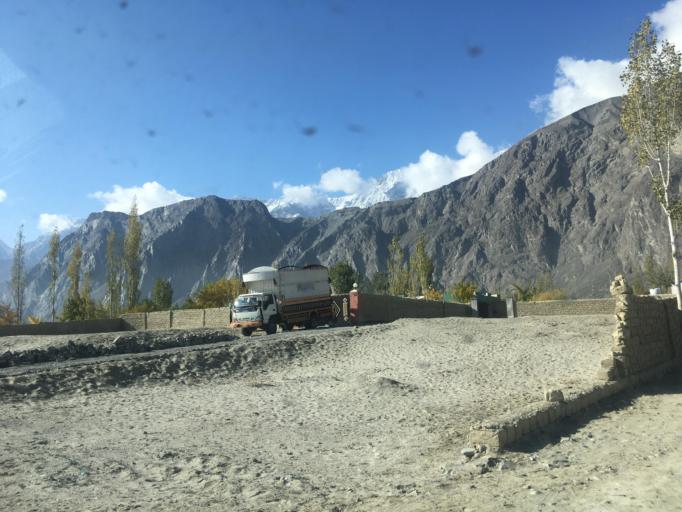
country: PK
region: Gilgit-Baltistan
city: Skardu
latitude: 35.3545
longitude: 75.5216
